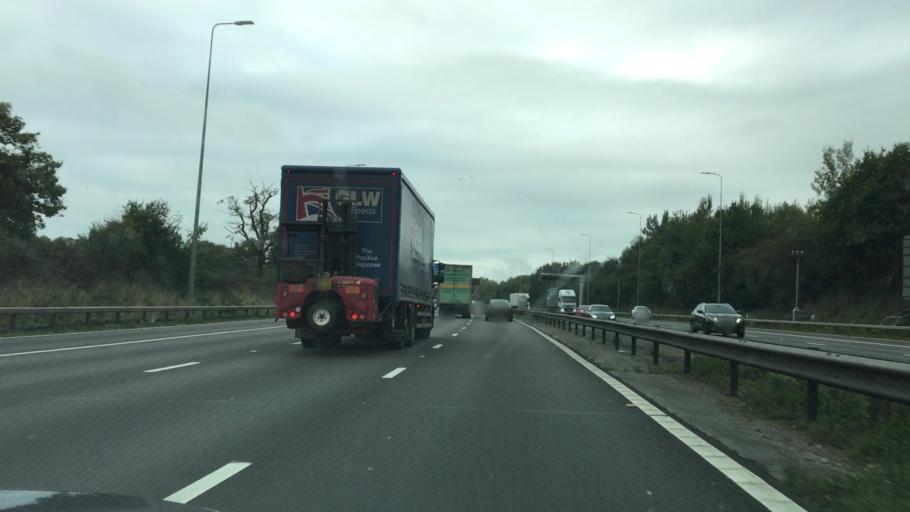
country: GB
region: England
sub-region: Solihull
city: Cheswick Green
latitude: 52.3651
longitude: -1.8013
